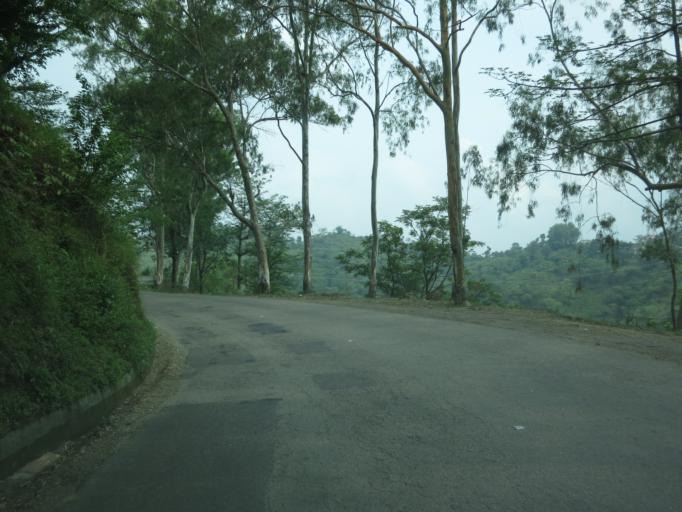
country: IN
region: Himachal Pradesh
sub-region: Bilaspur
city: Bilaspur
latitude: 31.2542
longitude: 76.8565
